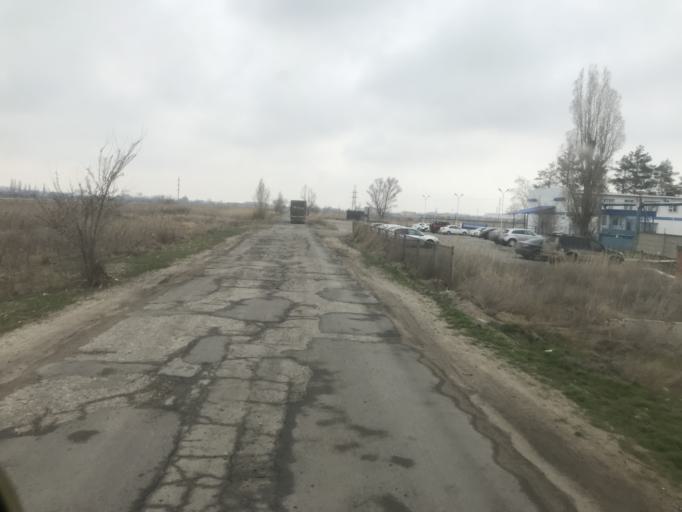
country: RU
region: Volgograd
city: Svetlyy Yar
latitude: 48.5155
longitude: 44.6315
